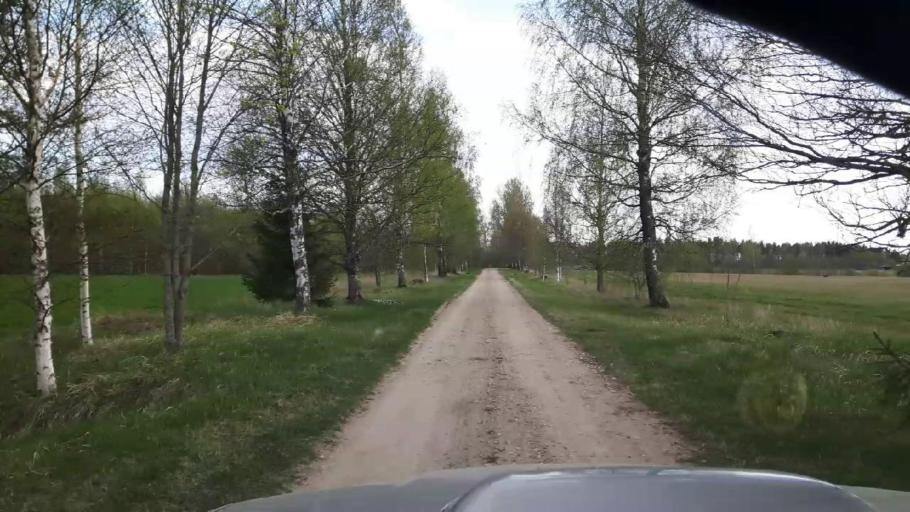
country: EE
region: Paernumaa
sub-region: Sindi linn
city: Sindi
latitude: 58.4279
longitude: 24.7608
